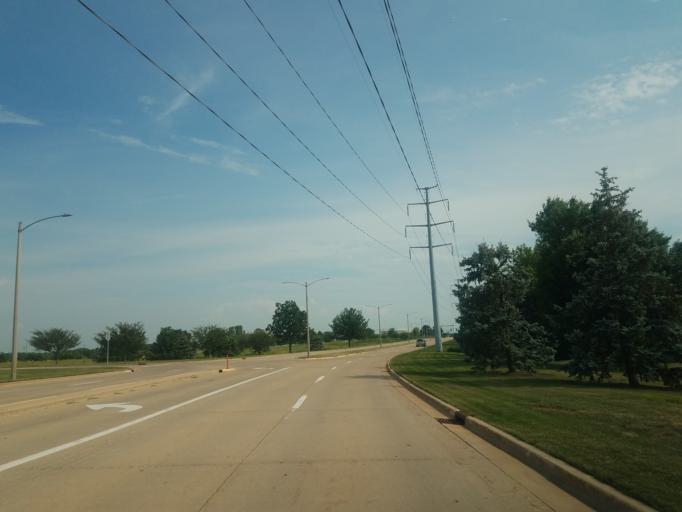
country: US
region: Illinois
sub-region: McLean County
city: Bloomington
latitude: 40.4577
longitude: -88.9622
